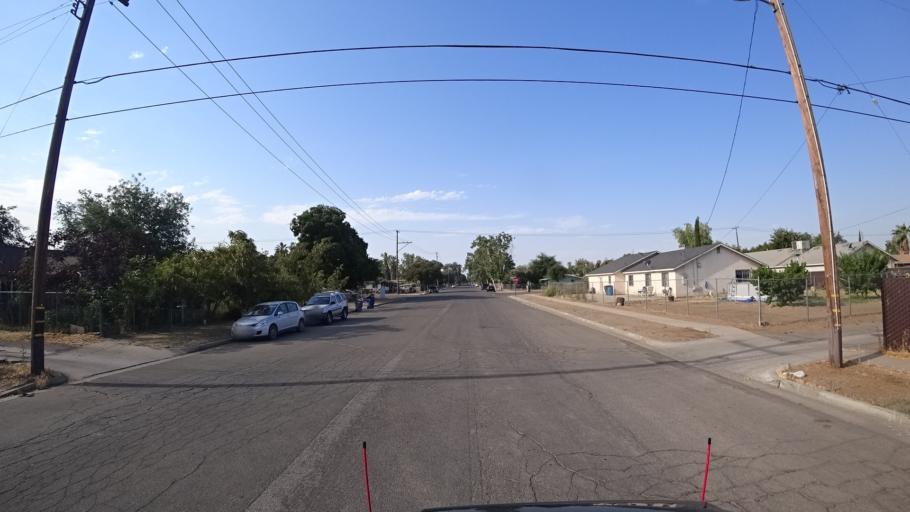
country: US
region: California
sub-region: Fresno County
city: Fresno
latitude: 36.7314
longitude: -119.8101
